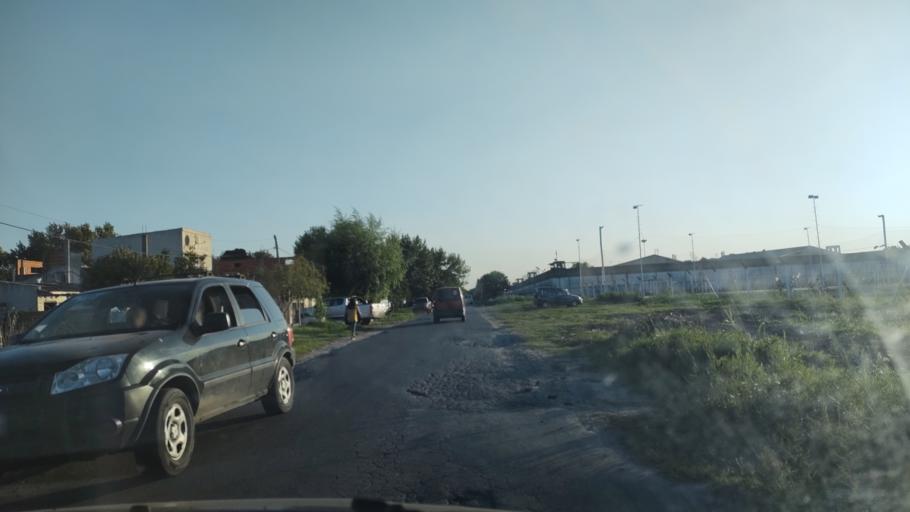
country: AR
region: Buenos Aires
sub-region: Partido de La Plata
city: La Plata
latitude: -34.9692
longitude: -57.9697
